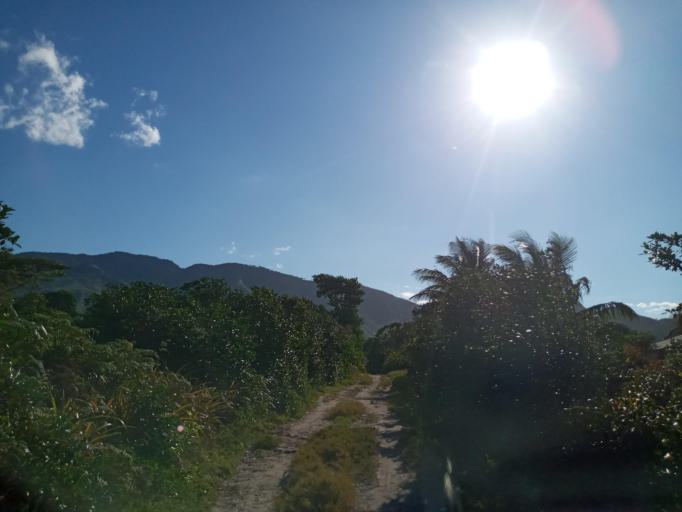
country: MG
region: Anosy
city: Fort Dauphin
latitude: -24.8275
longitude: 47.0466
